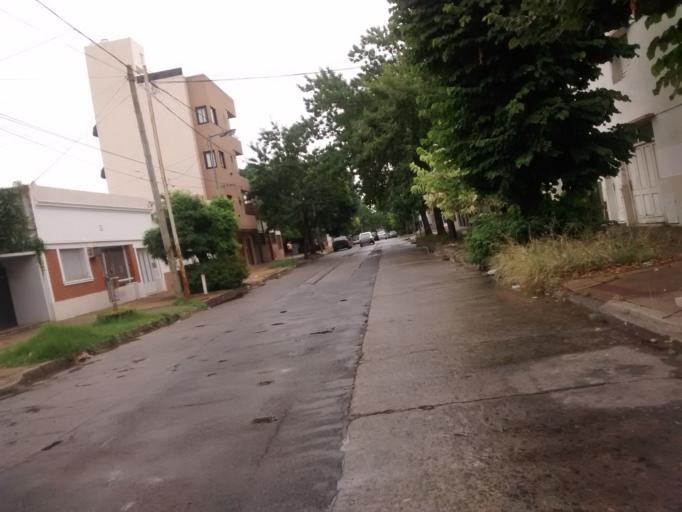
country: AR
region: Buenos Aires
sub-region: Partido de La Plata
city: La Plata
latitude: -34.9384
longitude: -57.9431
